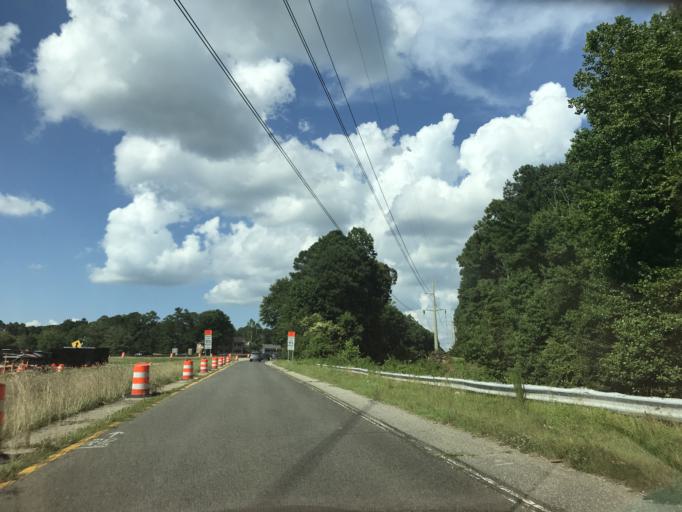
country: US
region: North Carolina
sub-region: Wake County
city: West Raleigh
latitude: 35.7706
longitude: -78.7213
